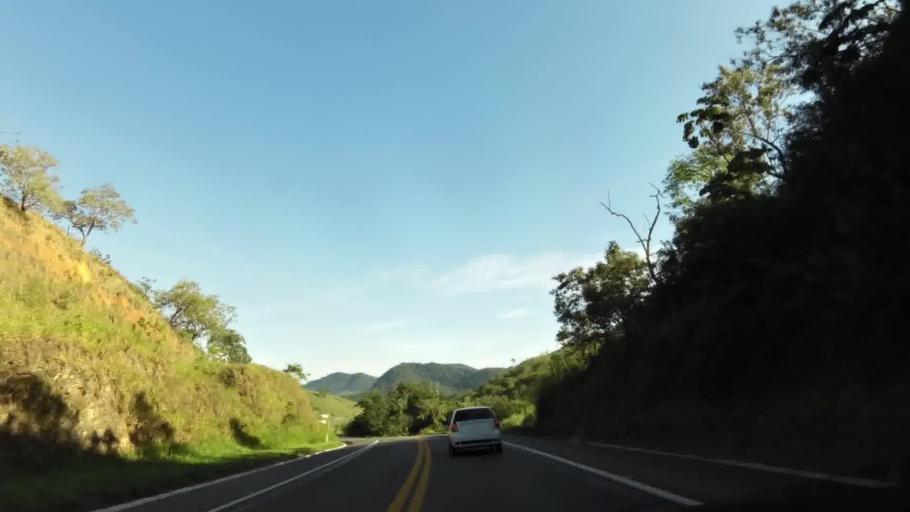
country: BR
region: Espirito Santo
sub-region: Viana
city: Viana
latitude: -20.3975
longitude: -40.4573
